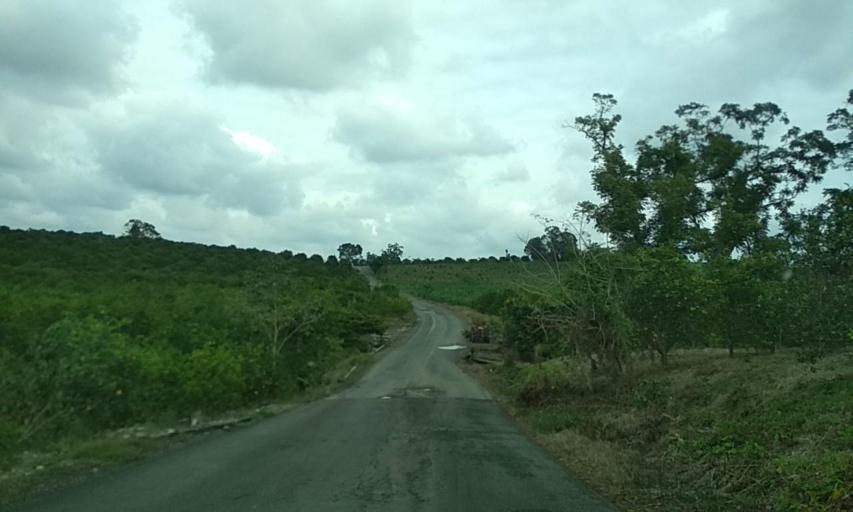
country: MX
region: Veracruz
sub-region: Papantla
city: El Chote
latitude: 20.3362
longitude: -97.3984
